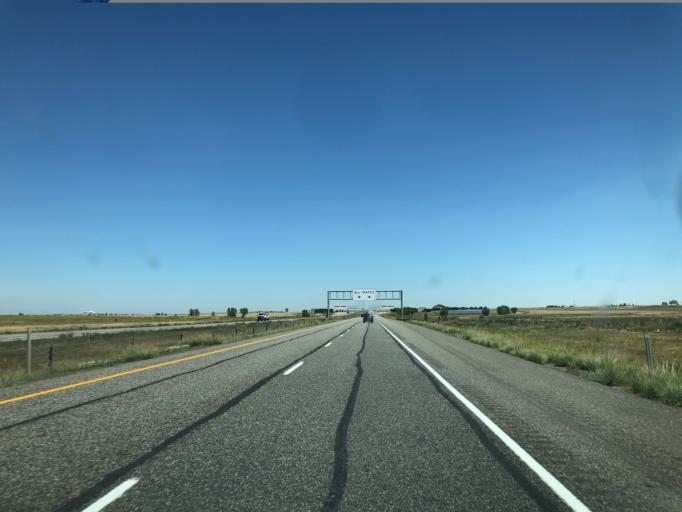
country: US
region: Colorado
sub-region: Adams County
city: Aurora
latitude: 39.7621
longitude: -104.7164
